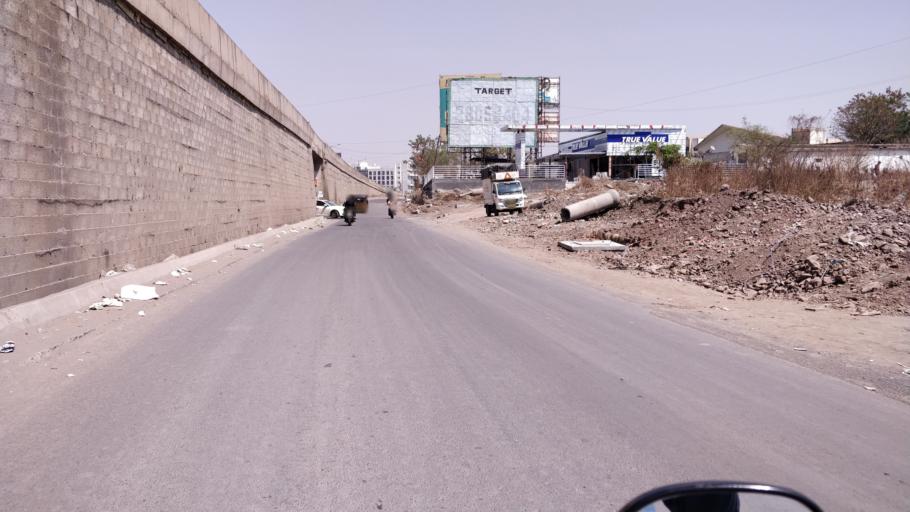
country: IN
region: Maharashtra
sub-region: Pune Division
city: Kharakvasla
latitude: 18.5153
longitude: 73.7693
